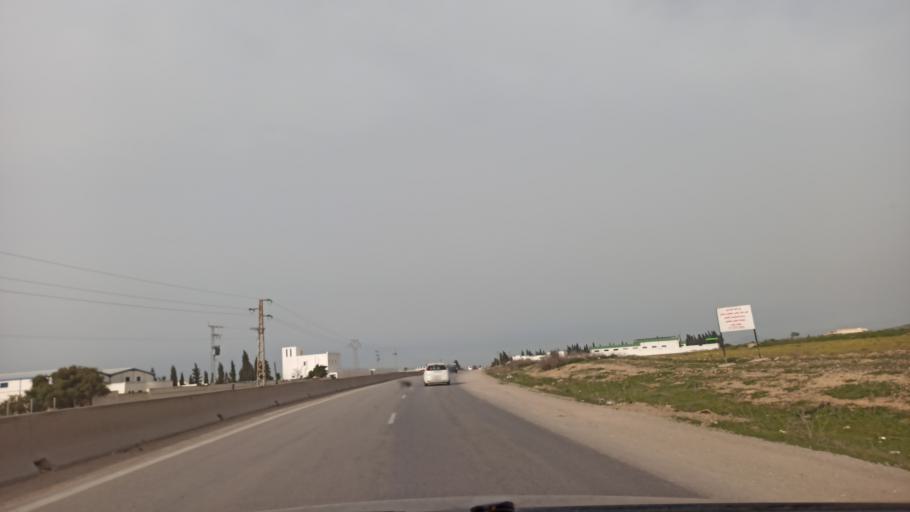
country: TN
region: Tunis
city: La Mohammedia
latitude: 36.5685
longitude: 10.0846
